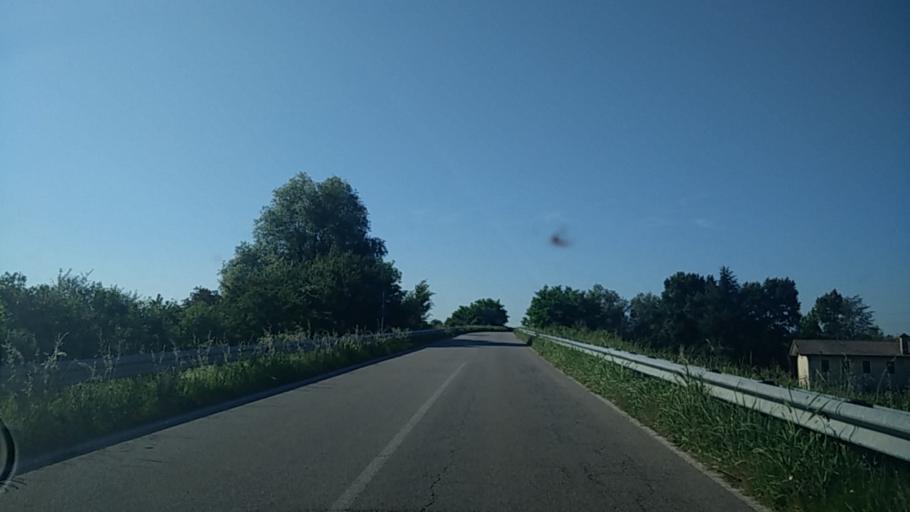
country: IT
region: Veneto
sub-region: Provincia di Venezia
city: Dolo
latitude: 45.4069
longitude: 12.0826
